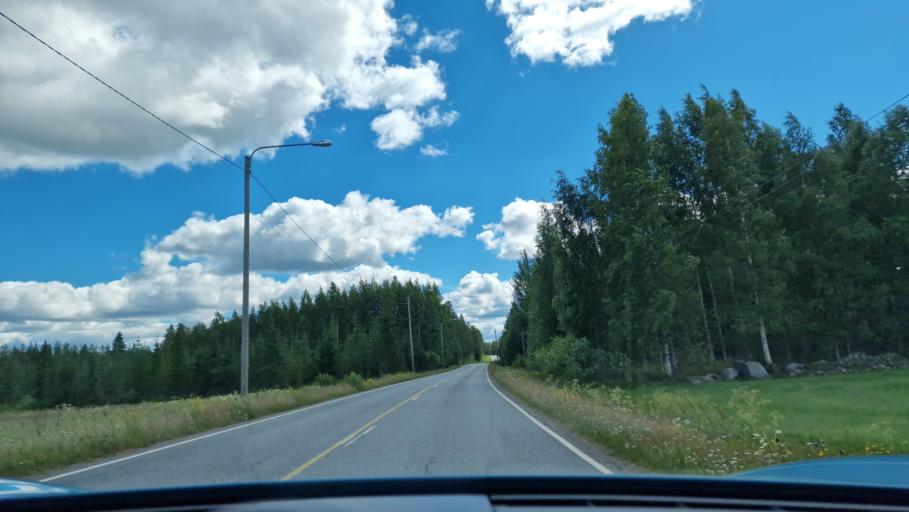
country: FI
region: Southern Ostrobothnia
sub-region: Jaerviseutu
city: Soini
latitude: 62.8417
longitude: 24.3286
